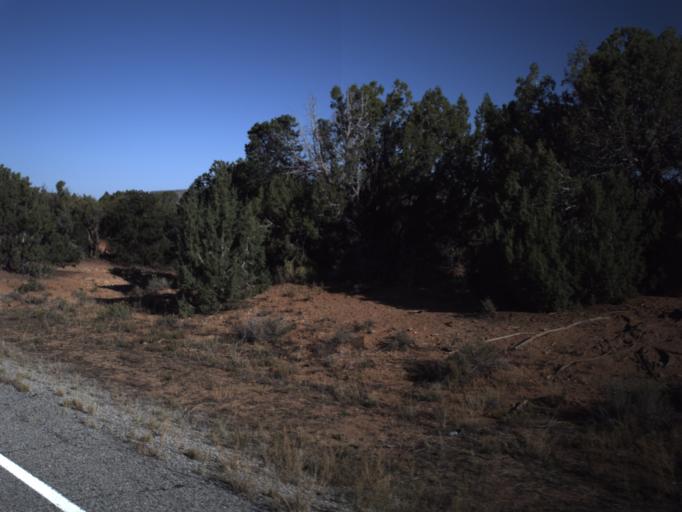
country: US
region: Utah
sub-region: San Juan County
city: Blanding
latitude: 37.5431
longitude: -109.9786
